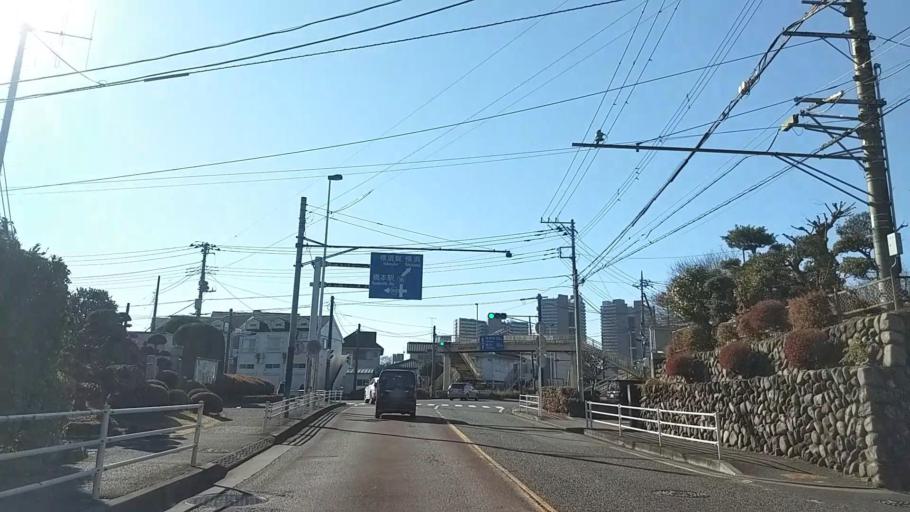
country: JP
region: Tokyo
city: Hachioji
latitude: 35.6014
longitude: 139.3405
